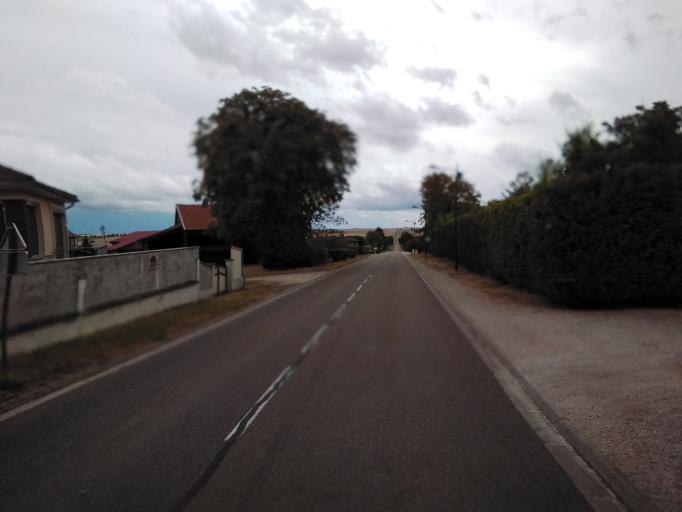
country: FR
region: Champagne-Ardenne
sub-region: Departement de l'Aube
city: Brienne-le-Chateau
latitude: 48.5540
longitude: 4.5230
